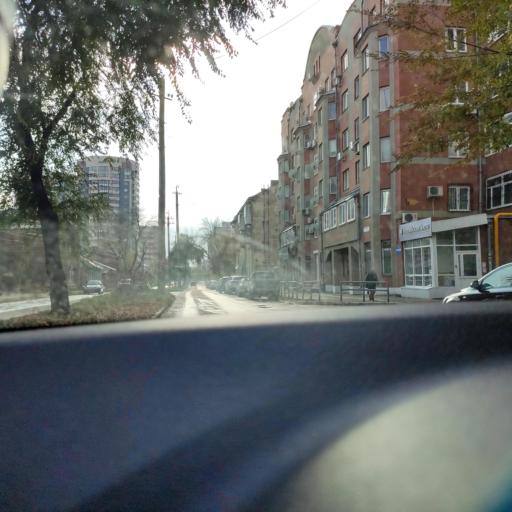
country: RU
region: Samara
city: Samara
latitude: 53.1972
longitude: 50.1134
